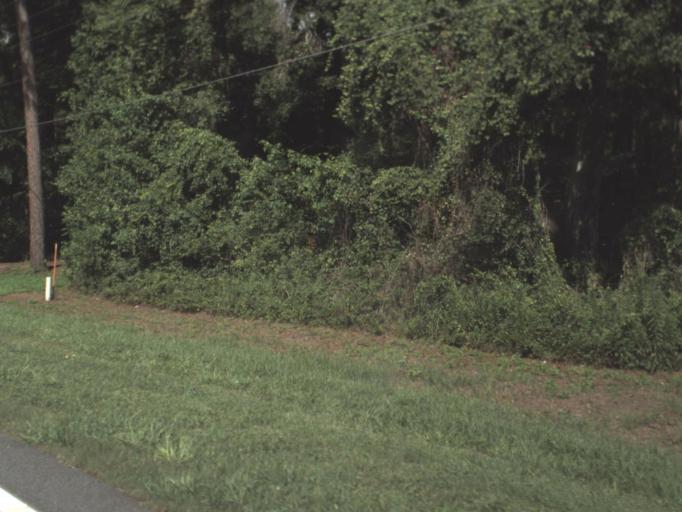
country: US
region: Florida
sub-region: Madison County
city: Madison
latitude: 30.5127
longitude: -83.3728
